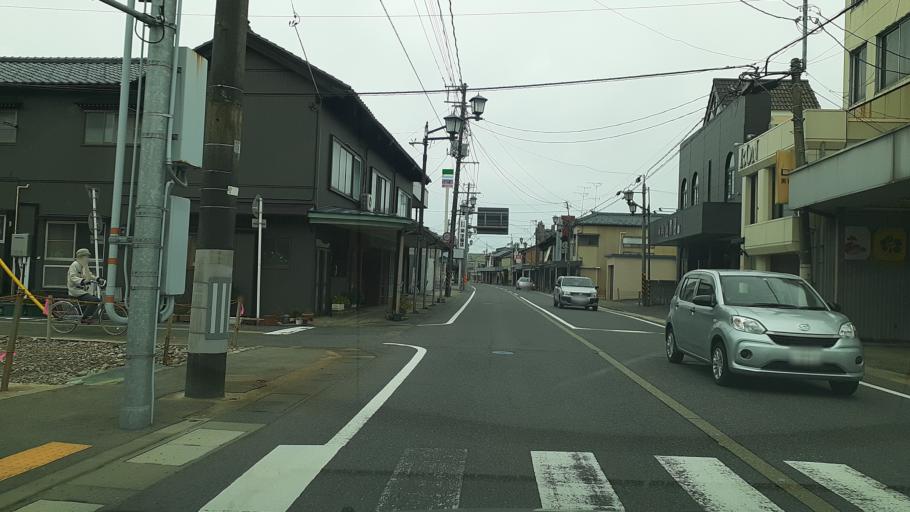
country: JP
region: Niigata
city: Gosen
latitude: 37.7416
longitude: 139.1758
